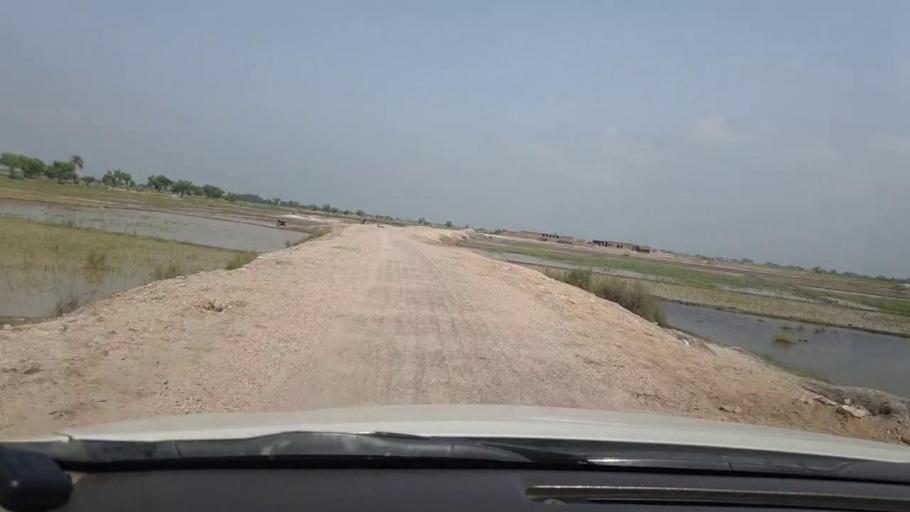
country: PK
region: Sindh
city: Shikarpur
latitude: 28.0000
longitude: 68.5596
